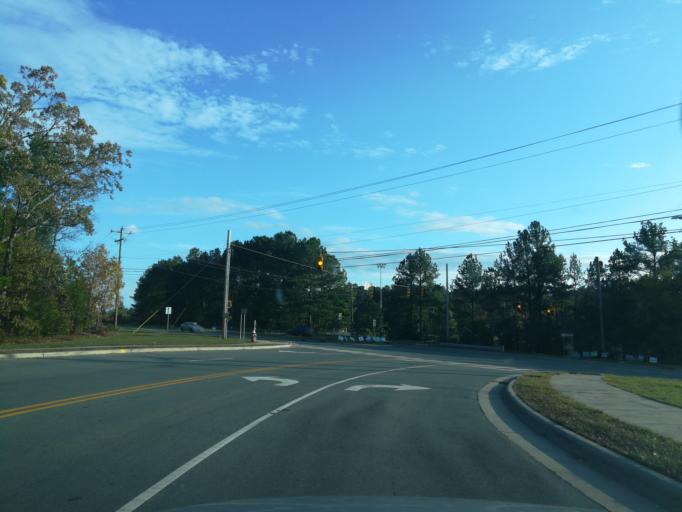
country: US
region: North Carolina
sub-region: Orange County
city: Chapel Hill
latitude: 35.9621
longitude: -79.0339
